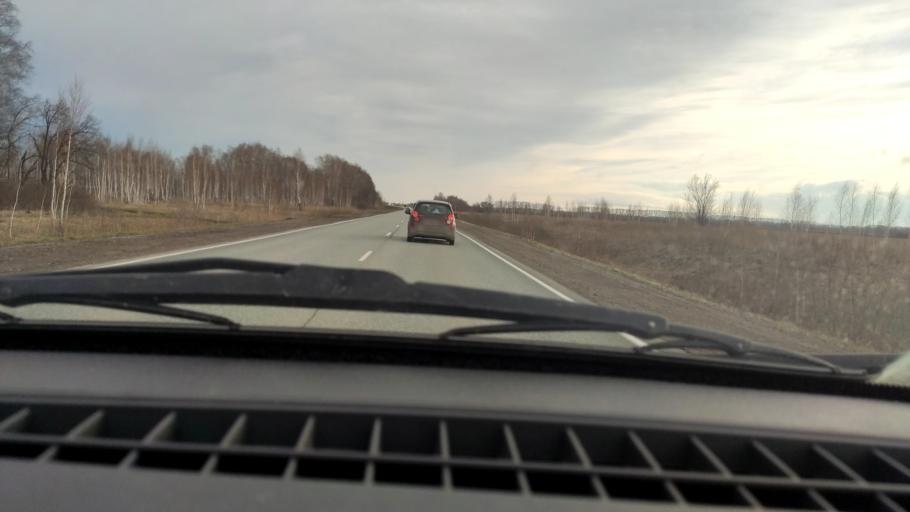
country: RU
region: Bashkortostan
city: Chishmy
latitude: 54.4179
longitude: 55.2262
